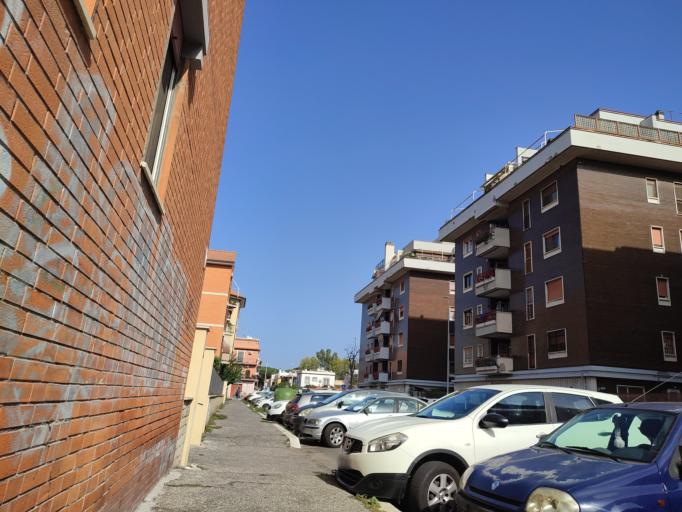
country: IT
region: Latium
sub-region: Citta metropolitana di Roma Capitale
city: Lido di Ostia
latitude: 41.7359
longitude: 12.2941
